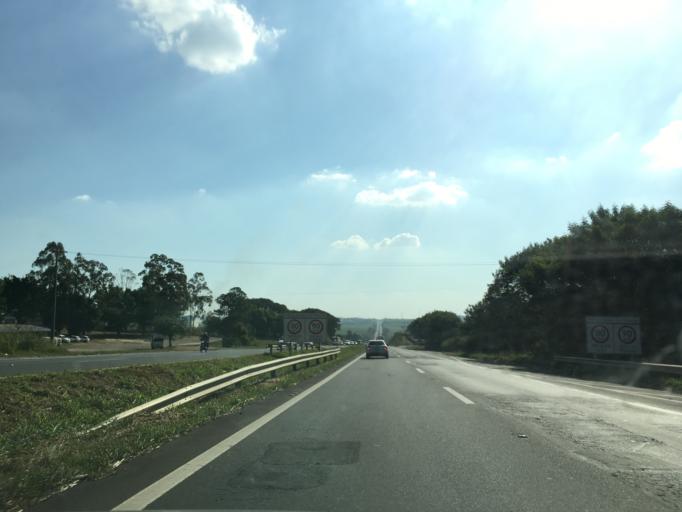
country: BR
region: Sao Paulo
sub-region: Santa Barbara D'Oeste
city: Santa Barbara d'Oeste
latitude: -22.7594
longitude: -47.4659
